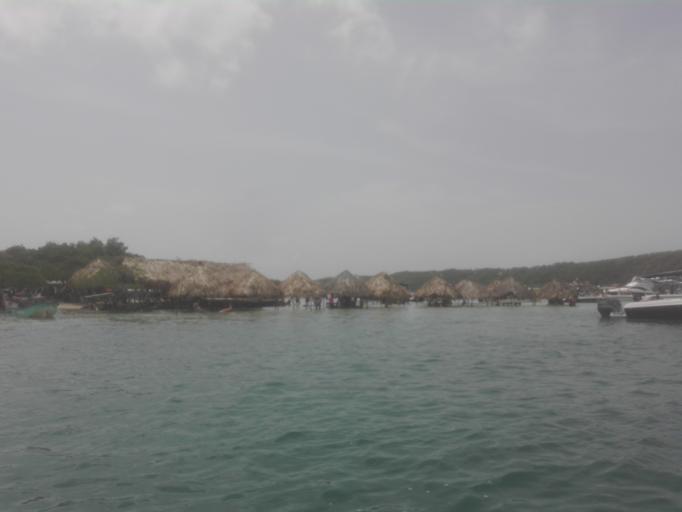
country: CO
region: Bolivar
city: Turbana
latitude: 10.1641
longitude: -75.6697
